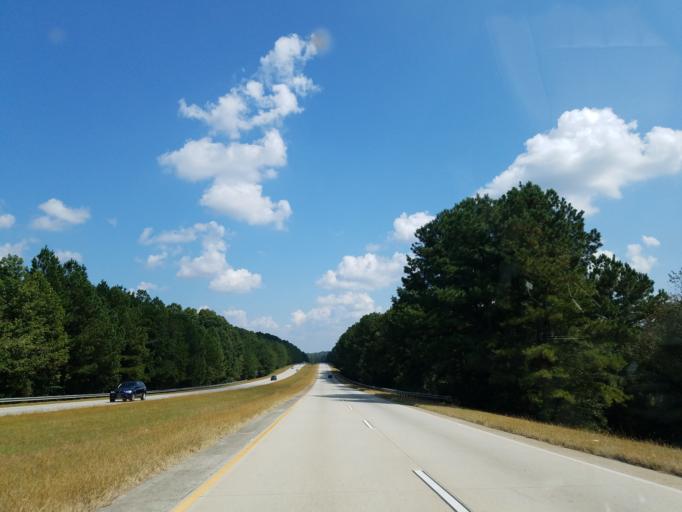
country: US
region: Georgia
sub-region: Barrow County
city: Russell
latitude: 33.9517
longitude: -83.6866
